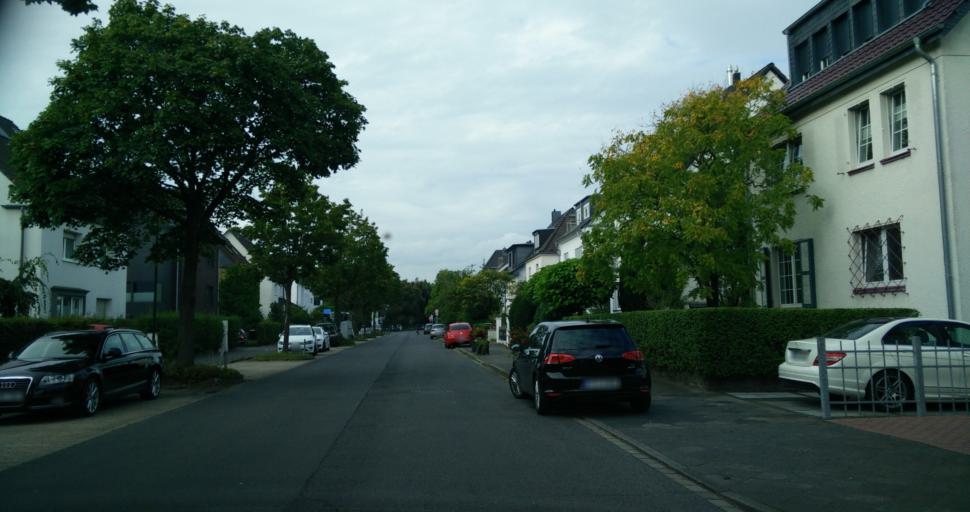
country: DE
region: North Rhine-Westphalia
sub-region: Regierungsbezirk Dusseldorf
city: Meerbusch
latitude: 51.2951
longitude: 6.7410
